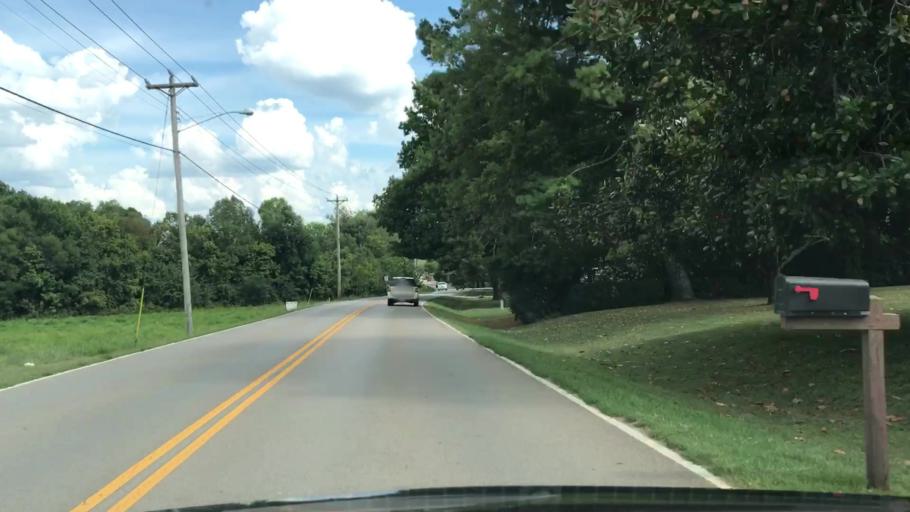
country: US
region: Tennessee
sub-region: Maury County
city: Spring Hill
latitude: 35.7458
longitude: -86.9321
